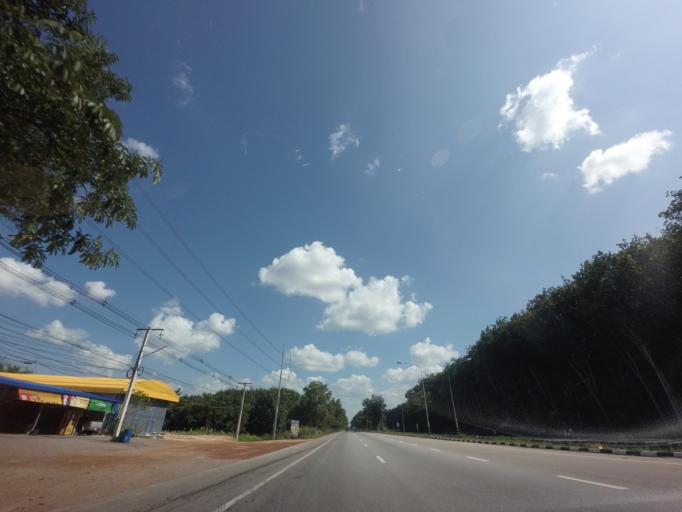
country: TH
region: Rayong
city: Wang Chan
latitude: 12.9596
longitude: 101.5044
